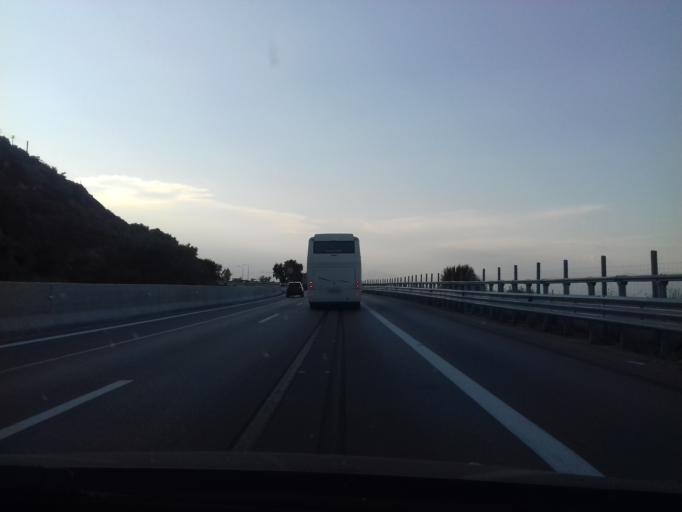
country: GR
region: West Greece
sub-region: Nomos Achaias
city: Siliveniotika
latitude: 38.1627
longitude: 22.3359
